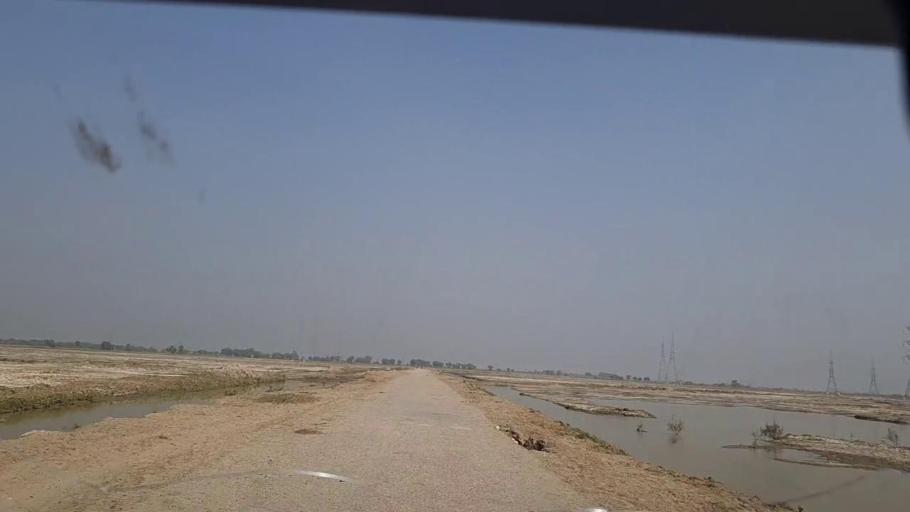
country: PK
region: Sindh
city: Shikarpur
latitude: 28.0321
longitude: 68.6281
